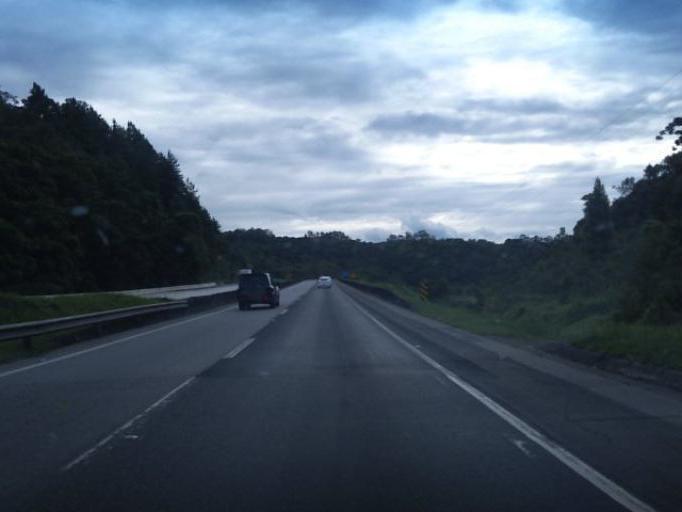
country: BR
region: Parana
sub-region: Campina Grande Do Sul
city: Campina Grande do Sul
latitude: -25.1670
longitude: -48.8650
